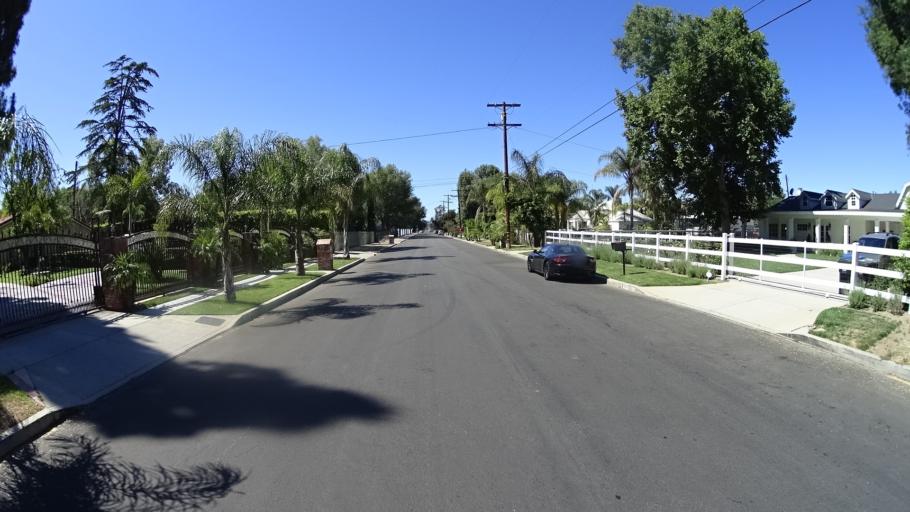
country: US
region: California
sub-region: Los Angeles County
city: San Fernando
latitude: 34.2487
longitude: -118.4609
